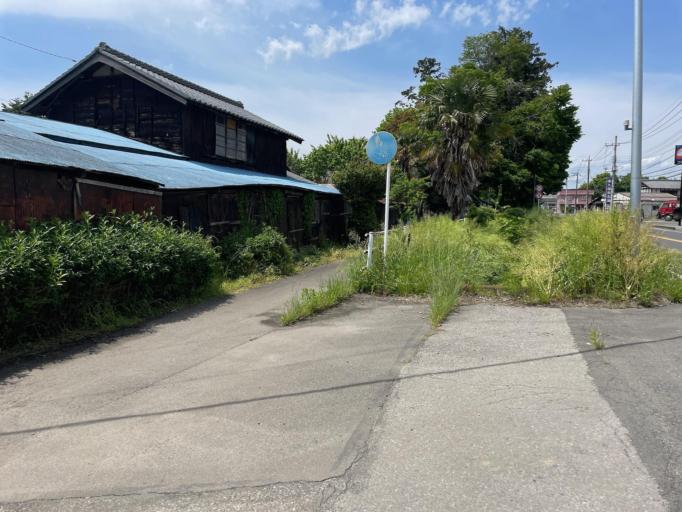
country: JP
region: Tochigi
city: Mibu
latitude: 36.4422
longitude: 139.7851
